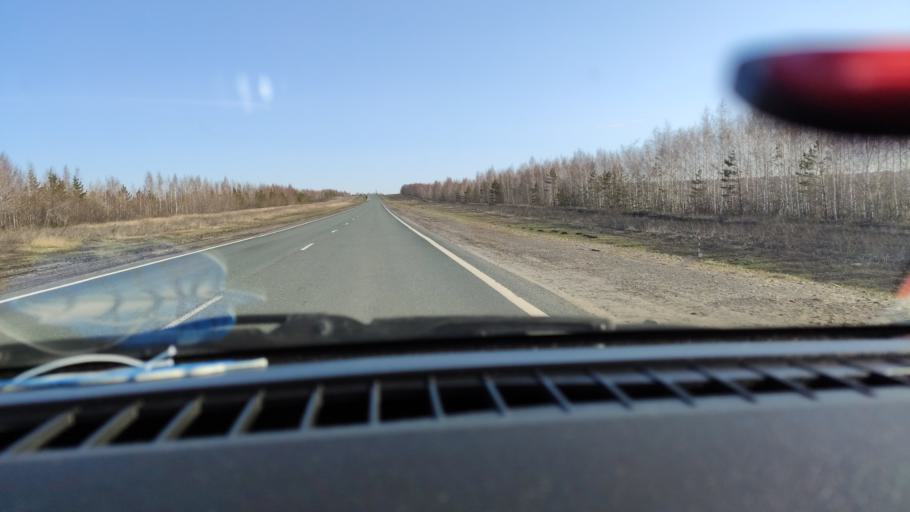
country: RU
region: Saratov
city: Dukhovnitskoye
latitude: 52.8275
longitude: 48.2374
